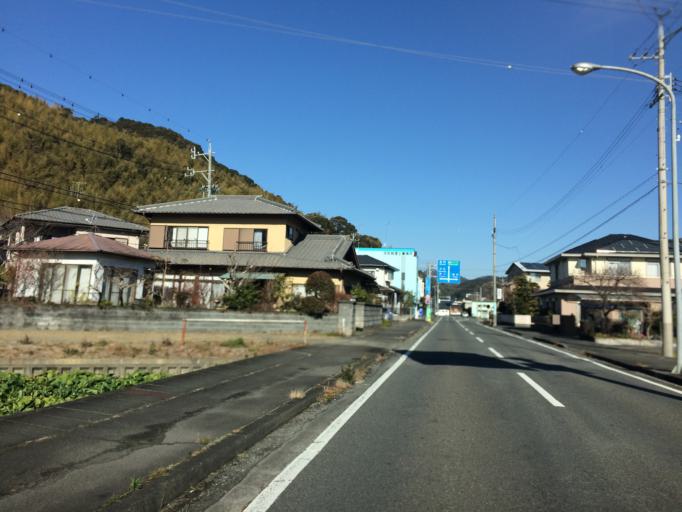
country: JP
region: Shizuoka
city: Shimada
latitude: 34.8375
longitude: 138.1998
